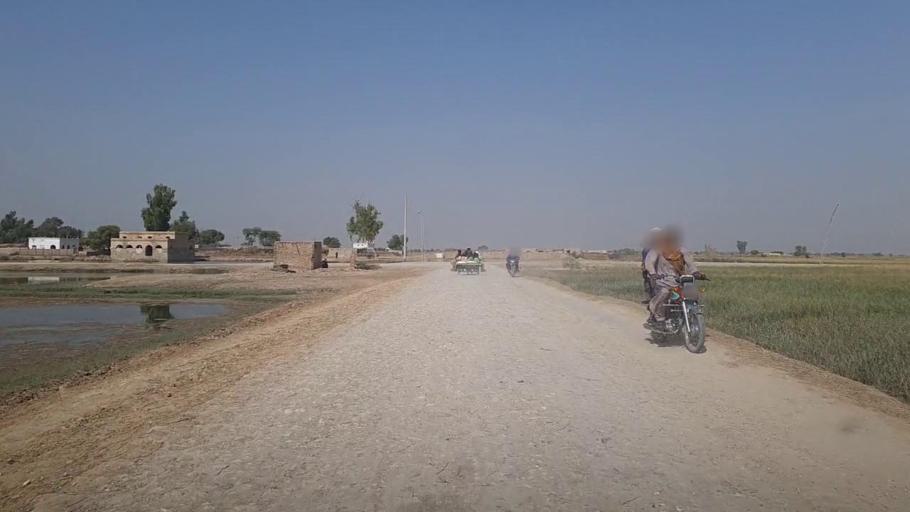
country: PK
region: Sindh
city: Kandhkot
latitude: 28.3945
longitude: 69.3261
